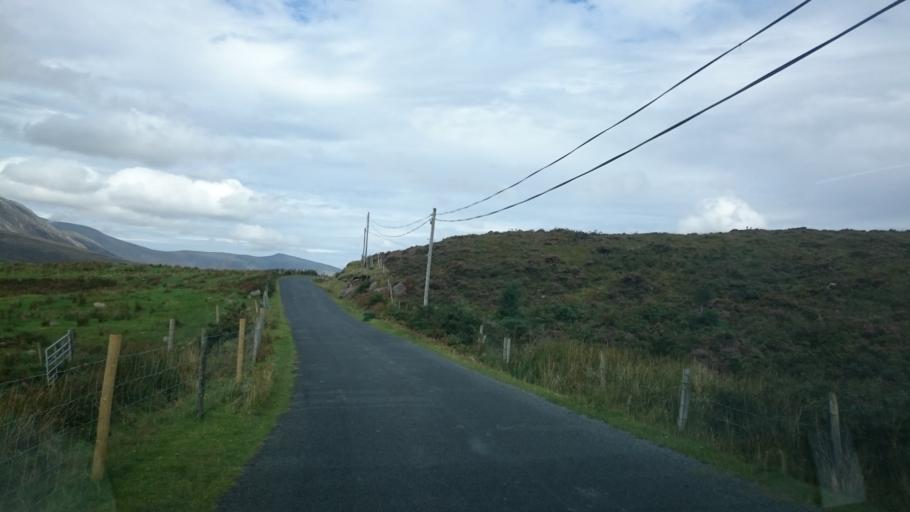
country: IE
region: Connaught
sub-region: Maigh Eo
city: Westport
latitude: 53.9299
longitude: -9.5650
